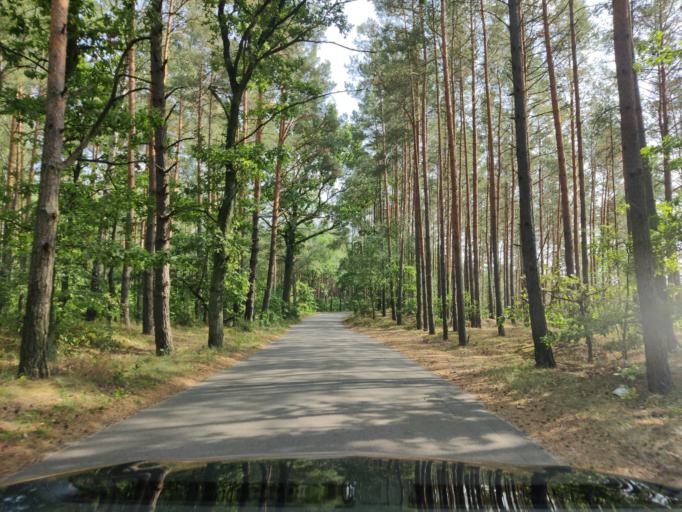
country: PL
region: Masovian Voivodeship
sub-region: Powiat makowski
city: Rozan
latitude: 52.8657
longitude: 21.4449
